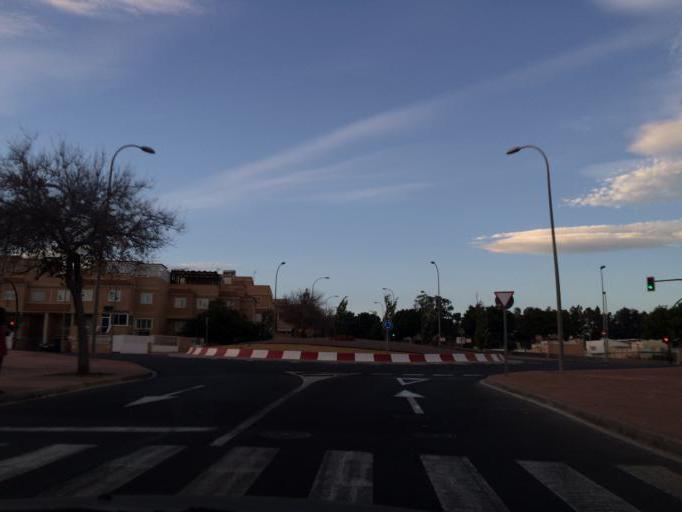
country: ES
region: Andalusia
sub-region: Provincia de Almeria
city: Almeria
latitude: 36.8575
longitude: -2.4424
